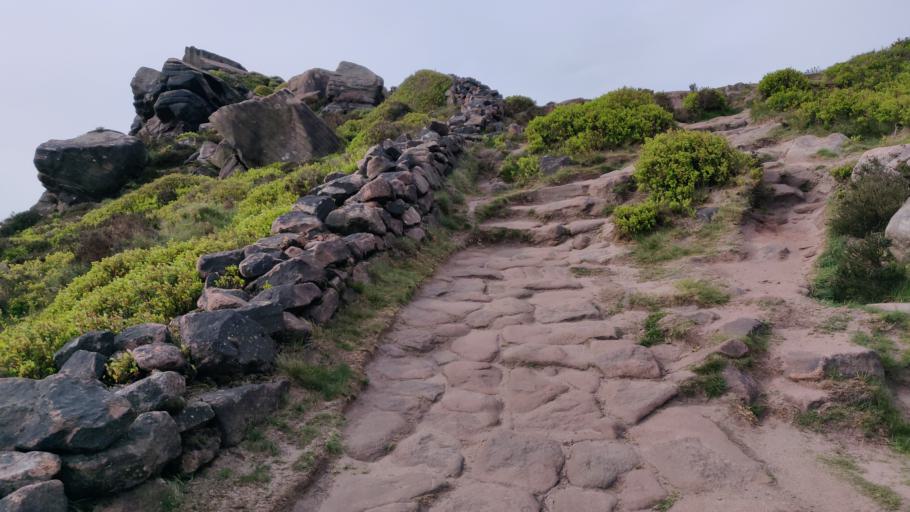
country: GB
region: England
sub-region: Staffordshire
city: Leek
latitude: 53.1595
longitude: -1.9939
